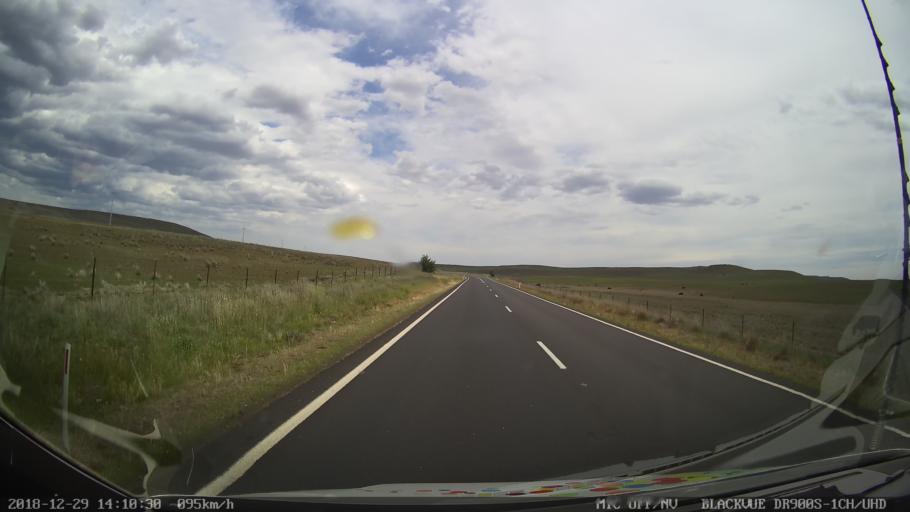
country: AU
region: New South Wales
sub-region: Cooma-Monaro
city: Cooma
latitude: -36.3926
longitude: 149.2172
